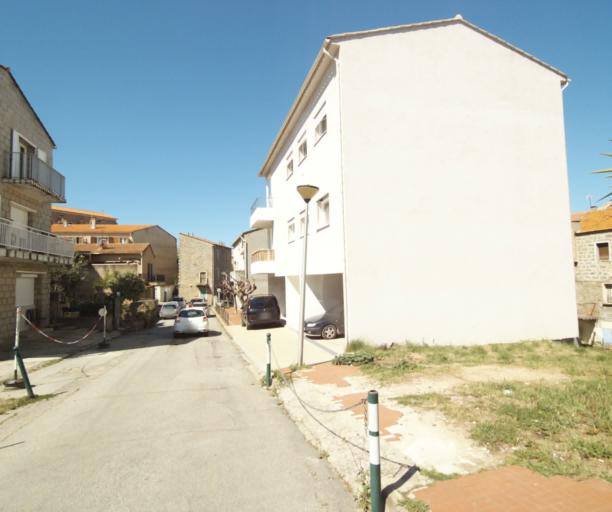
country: FR
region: Corsica
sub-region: Departement de la Corse-du-Sud
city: Propriano
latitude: 41.6758
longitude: 8.9061
